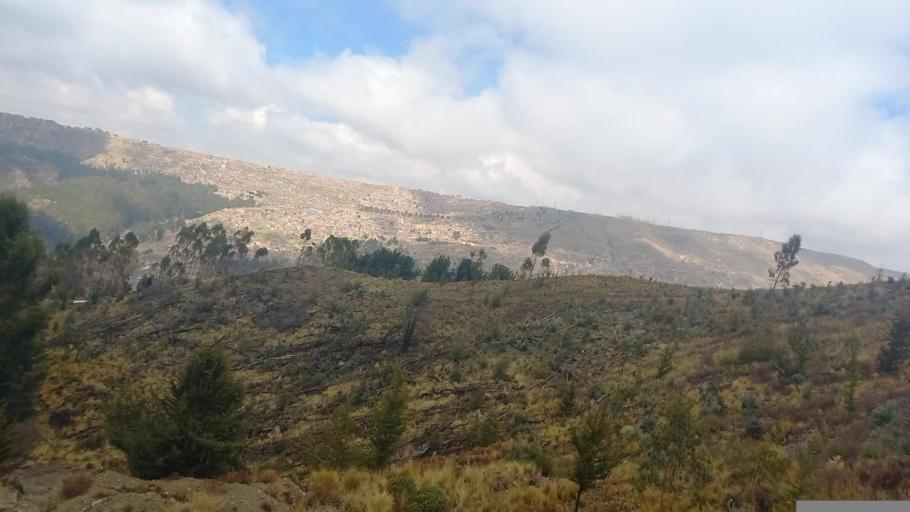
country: BO
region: La Paz
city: La Paz
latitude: -16.4669
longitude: -68.1429
